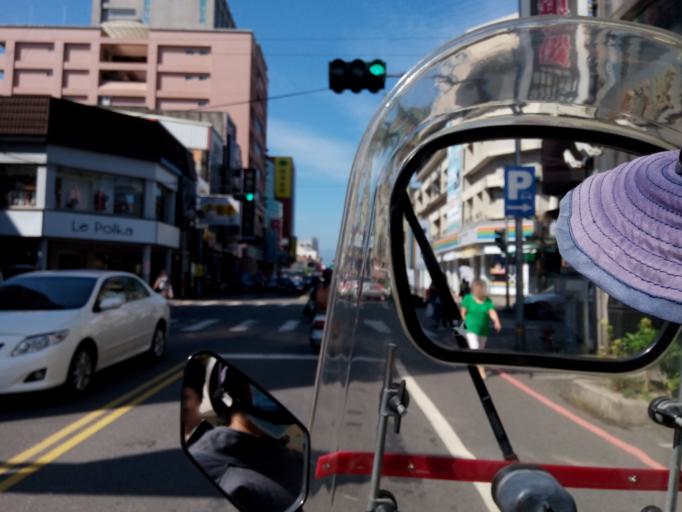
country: TW
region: Taiwan
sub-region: Yilan
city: Yilan
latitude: 24.6783
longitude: 121.7711
